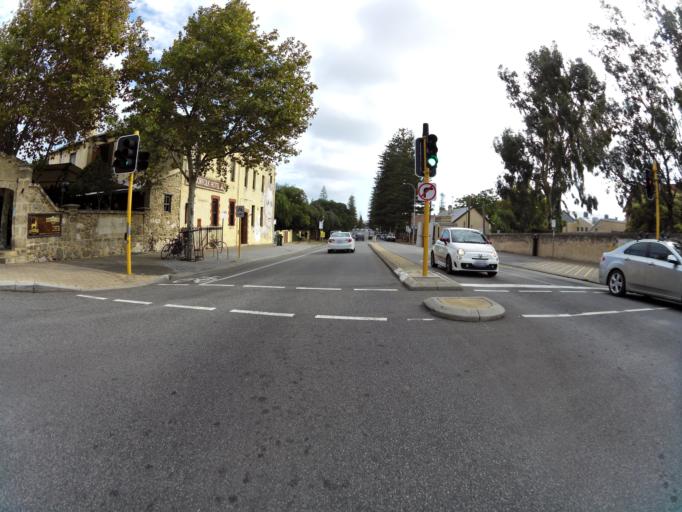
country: AU
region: Western Australia
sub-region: Fremantle
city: South Fremantle
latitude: -32.0568
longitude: 115.7495
